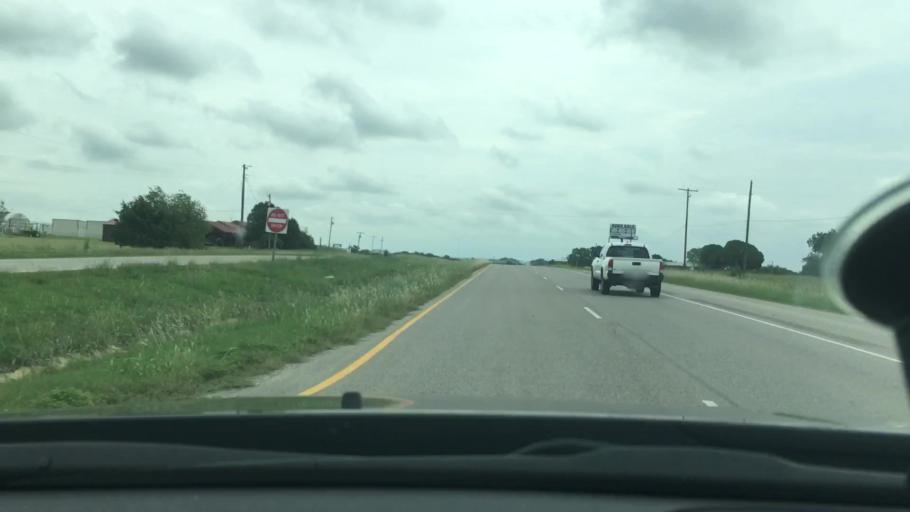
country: US
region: Oklahoma
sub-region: Carter County
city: Wilson
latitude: 34.1729
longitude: -97.4437
